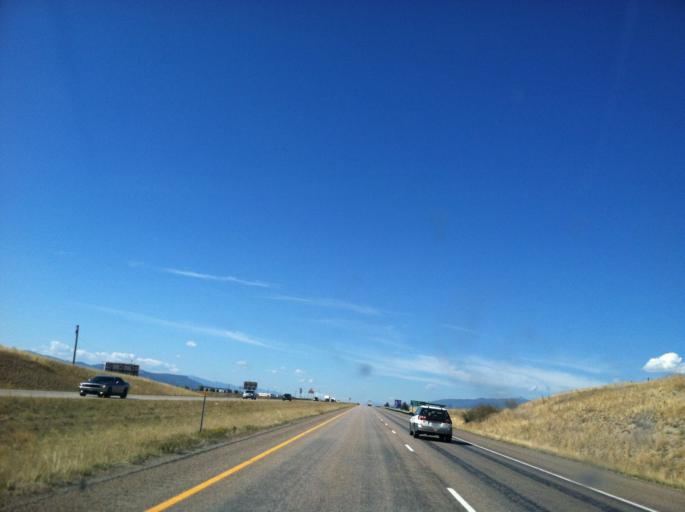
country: US
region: Montana
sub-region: Missoula County
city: Orchard Homes
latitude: 46.9425
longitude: -114.1156
